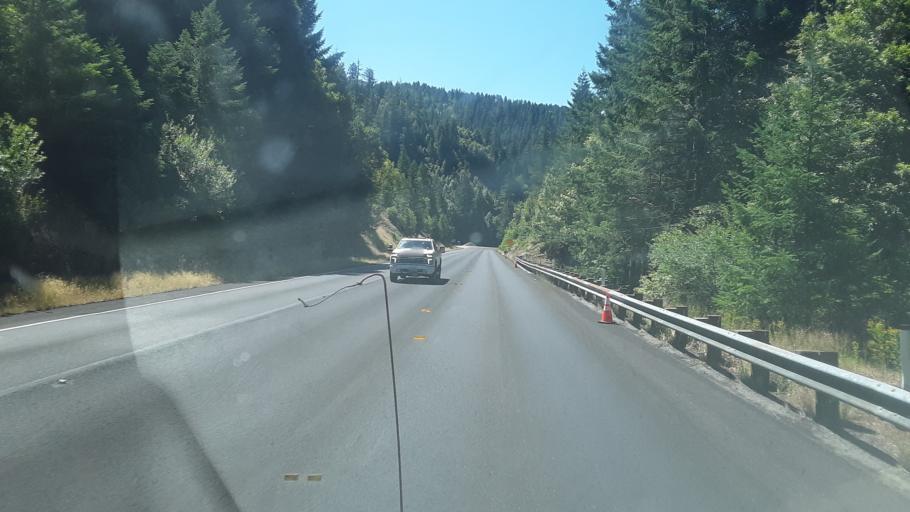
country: US
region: Oregon
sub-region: Josephine County
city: Cave Junction
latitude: 41.9584
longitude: -123.7450
